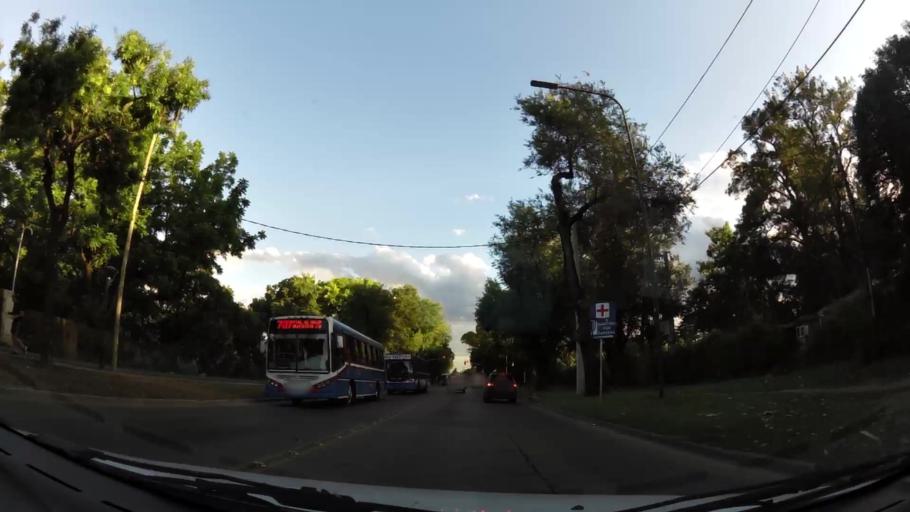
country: AR
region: Buenos Aires
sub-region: Partido de San Isidro
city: San Isidro
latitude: -34.4871
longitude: -58.5257
